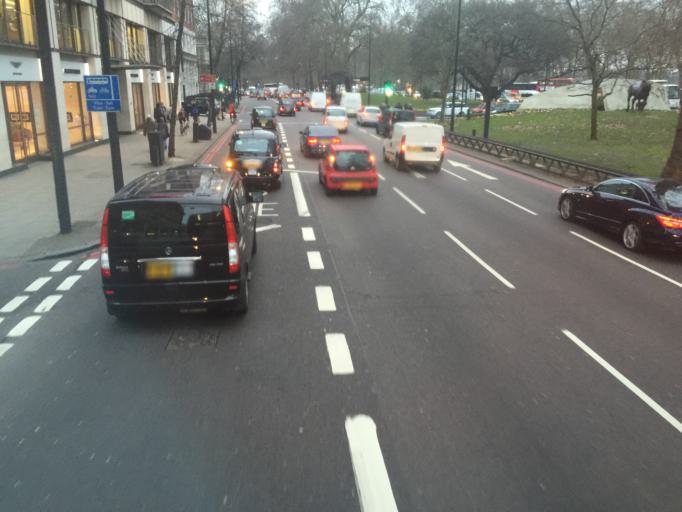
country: GB
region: England
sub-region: Greater London
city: Bayswater
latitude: 51.5117
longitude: -0.1574
